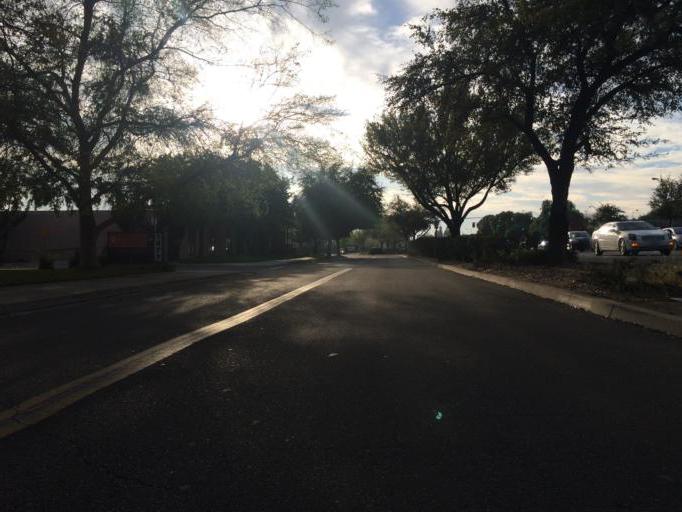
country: US
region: California
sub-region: Fresno County
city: Clovis
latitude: 36.8084
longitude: -119.7617
